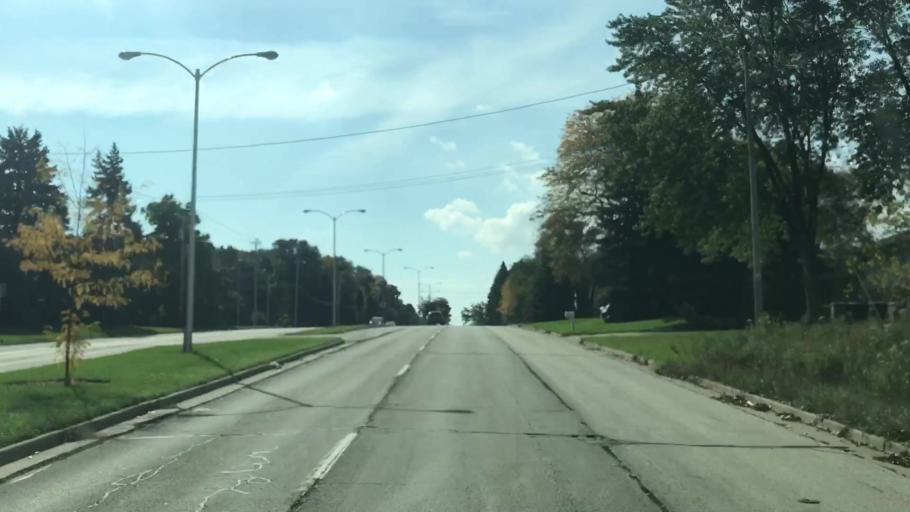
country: US
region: Wisconsin
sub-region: Waukesha County
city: Butler
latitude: 43.1567
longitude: -88.0449
